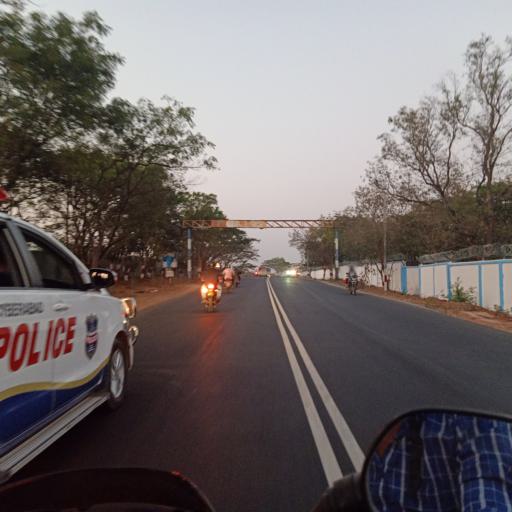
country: IN
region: Telangana
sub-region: Rangareddi
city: Secunderabad
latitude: 17.5527
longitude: 78.5362
